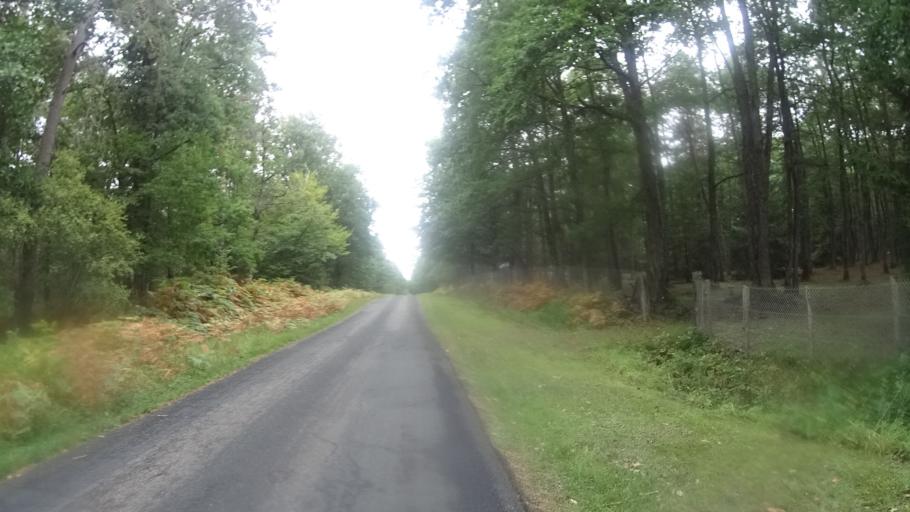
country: FR
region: Centre
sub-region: Departement du Loiret
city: Vitry-aux-Loges
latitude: 48.0254
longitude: 2.2589
